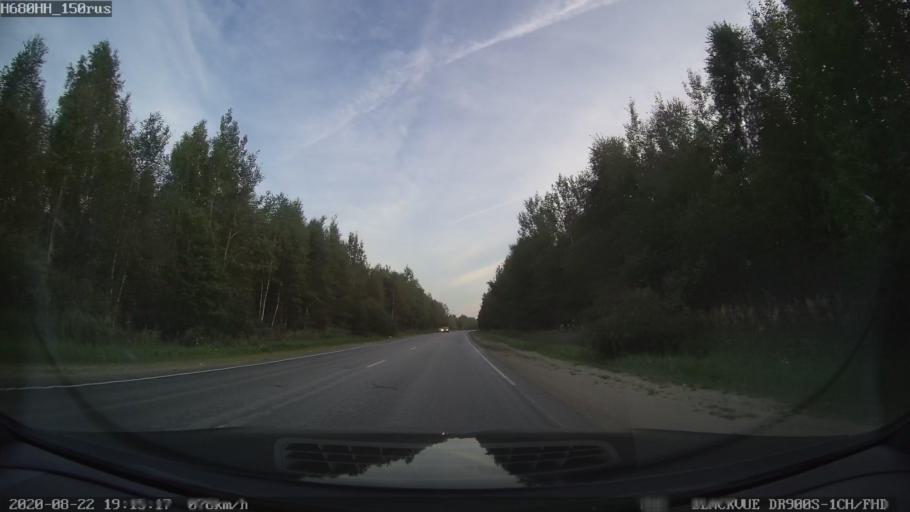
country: RU
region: Tverskaya
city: Sakharovo
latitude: 56.9696
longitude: 36.0229
